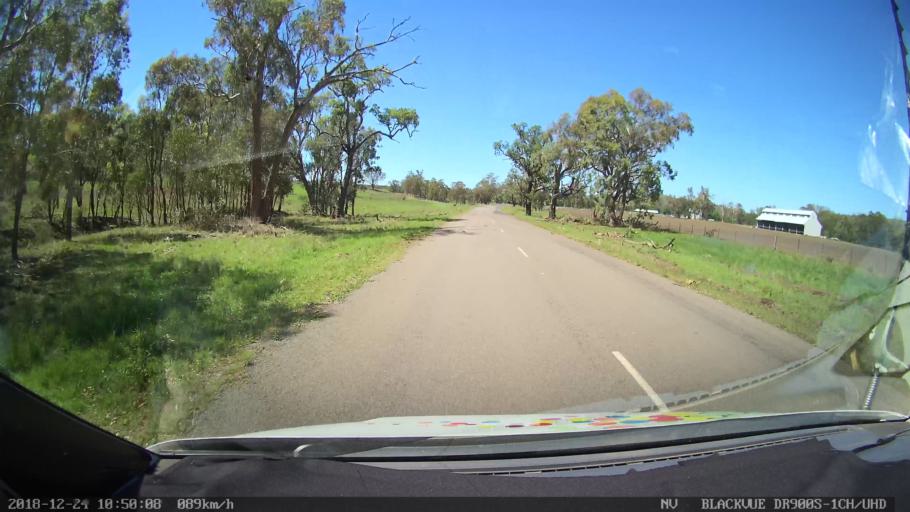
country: AU
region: New South Wales
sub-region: Upper Hunter Shire
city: Merriwa
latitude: -31.9564
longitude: 150.4246
